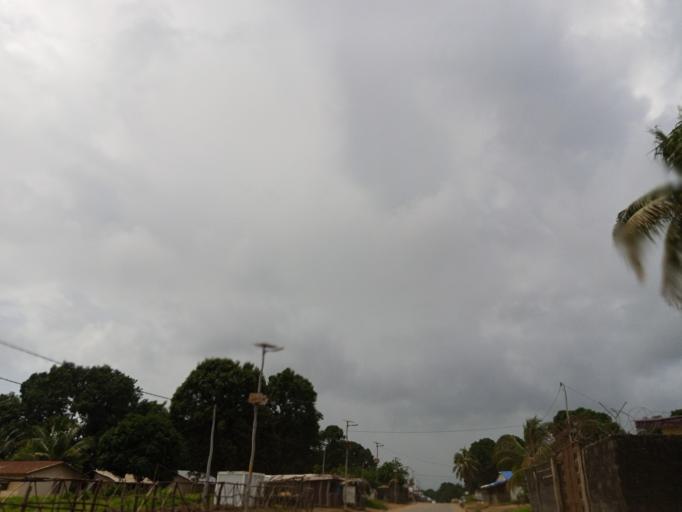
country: SL
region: Northern Province
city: Sawkta
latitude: 8.6263
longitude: -13.2065
